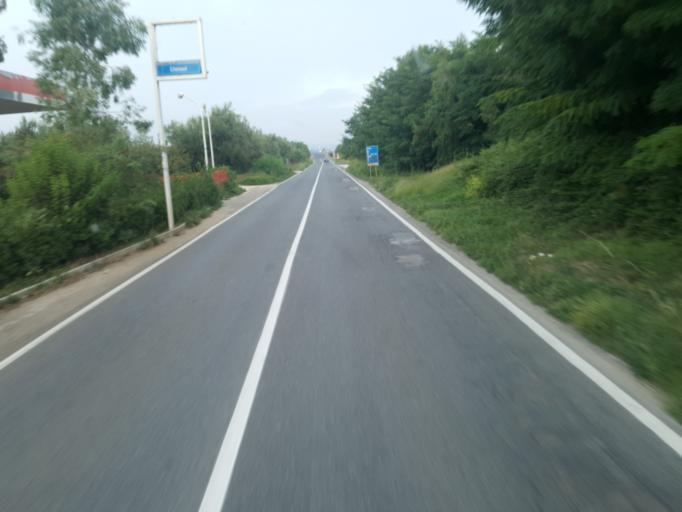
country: IT
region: Campania
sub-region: Provincia di Caserta
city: Pignataro Maggiore
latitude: 41.1703
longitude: 14.1439
